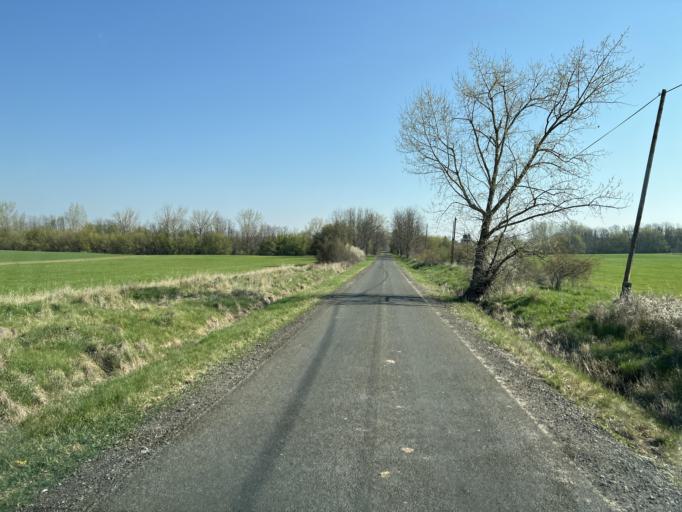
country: SK
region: Nitriansky
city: Sahy
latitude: 48.0304
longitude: 18.8326
